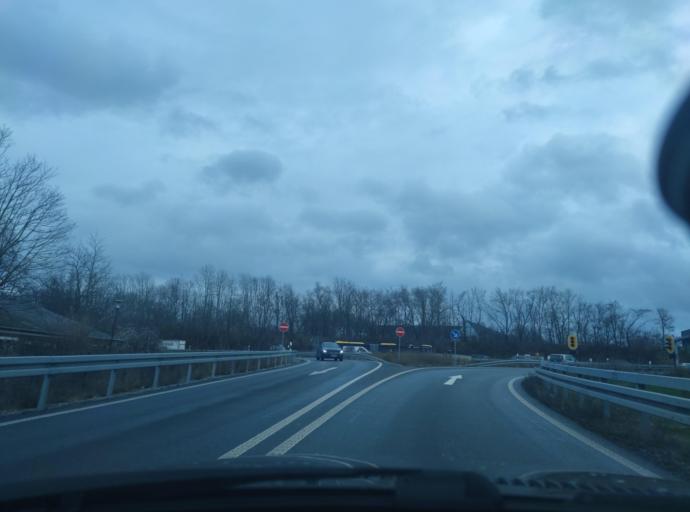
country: DE
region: North Rhine-Westphalia
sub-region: Regierungsbezirk Dusseldorf
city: Essen
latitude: 51.4616
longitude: 7.0560
